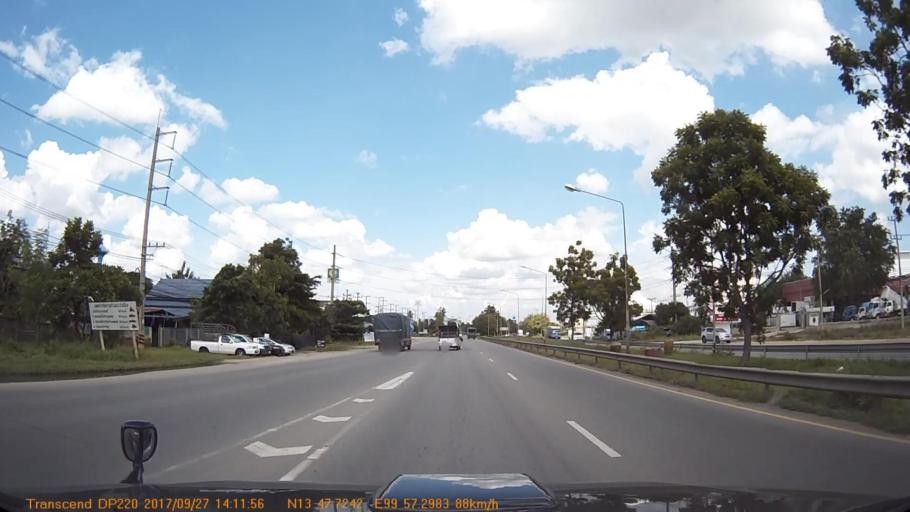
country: TH
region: Ratchaburi
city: Ban Pong
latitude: 13.7954
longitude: 99.9550
